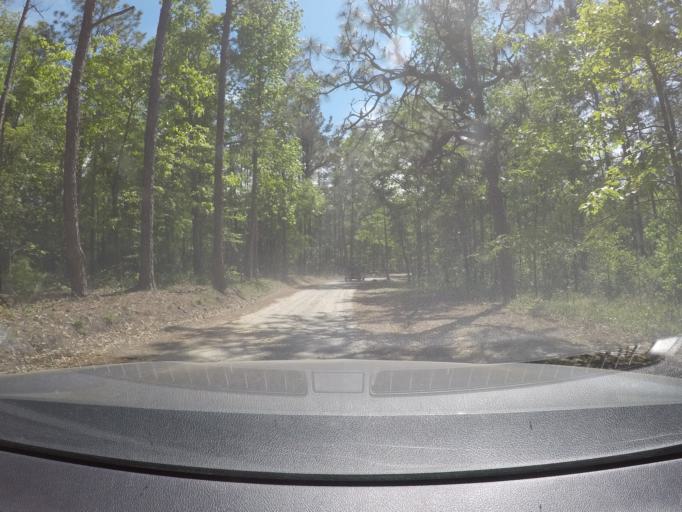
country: US
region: Georgia
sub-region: Evans County
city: Claxton
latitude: 32.1270
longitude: -81.7966
